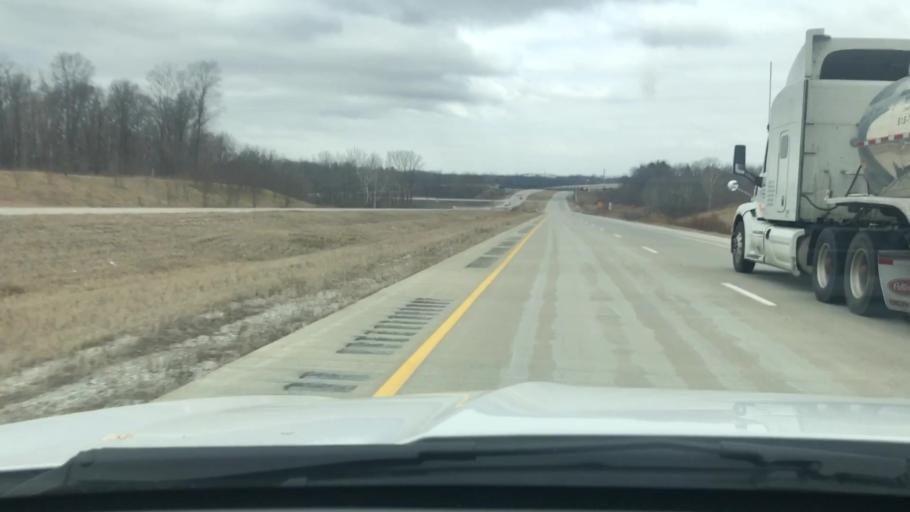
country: US
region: Indiana
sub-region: Carroll County
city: Delphi
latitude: 40.5878
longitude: -86.6514
